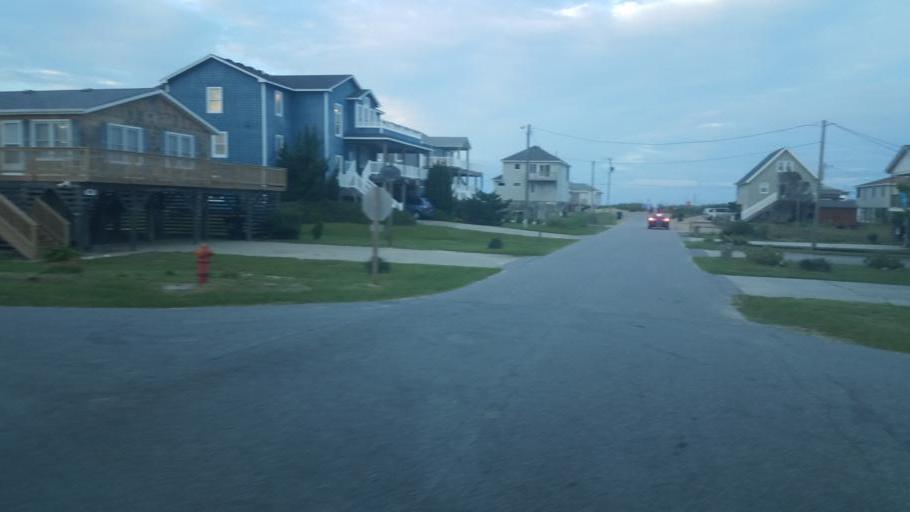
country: US
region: North Carolina
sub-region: Dare County
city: Kitty Hawk
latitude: 36.0954
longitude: -75.7101
